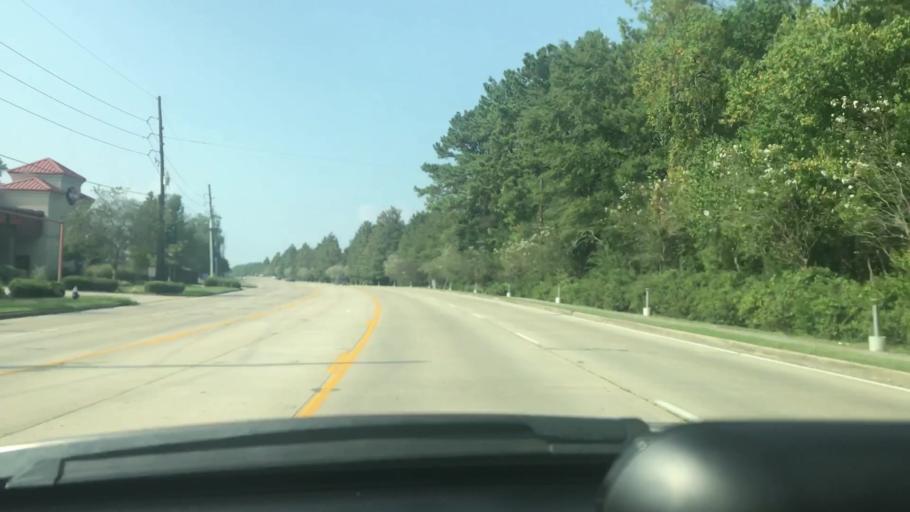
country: US
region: Louisiana
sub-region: Tangipahoa Parish
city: Hammond
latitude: 30.4884
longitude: -90.4567
